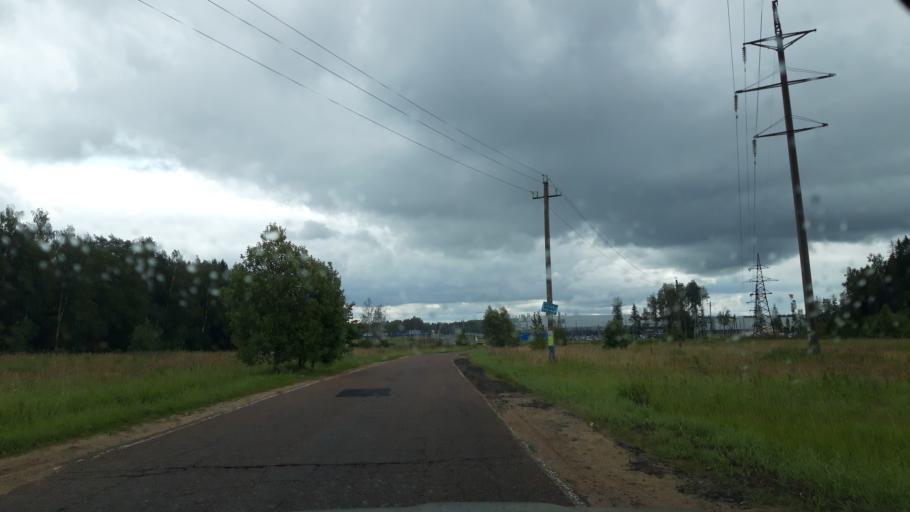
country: RU
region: Moskovskaya
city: Lozhki
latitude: 56.0902
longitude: 37.0766
